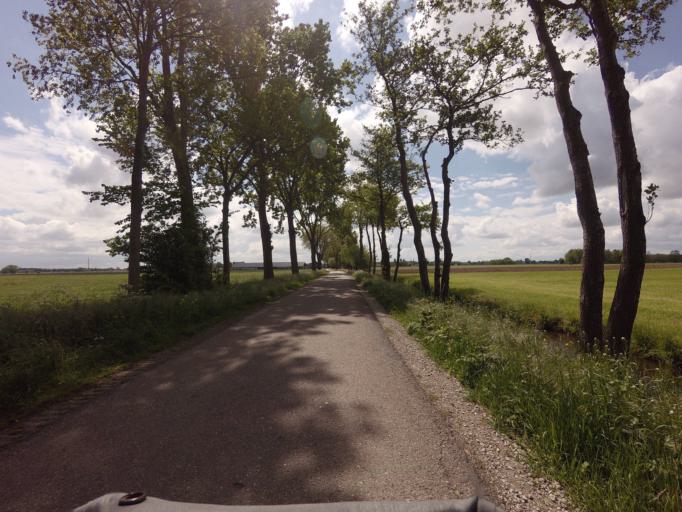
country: NL
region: South Holland
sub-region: Gemeente Gorinchem
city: Gorinchem
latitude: 51.8602
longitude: 4.9397
